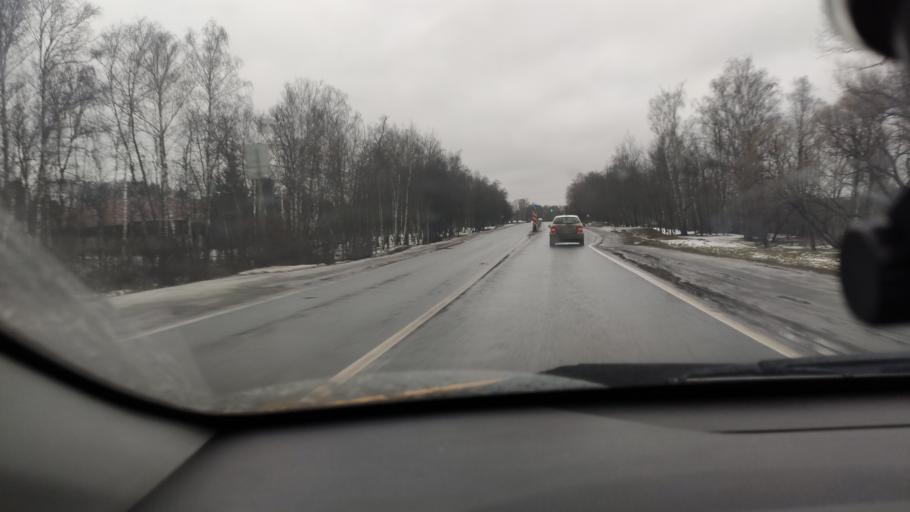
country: RU
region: Moskovskaya
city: Troitsk
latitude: 55.2981
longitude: 37.1978
